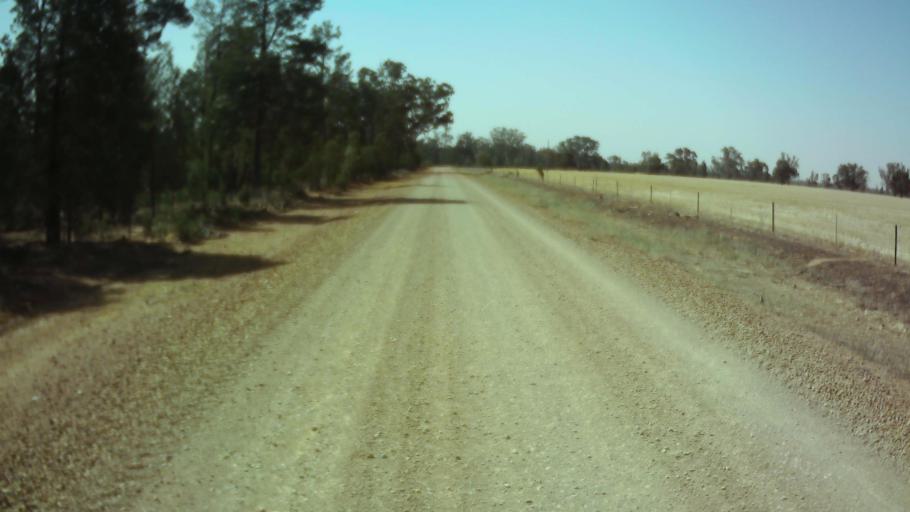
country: AU
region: New South Wales
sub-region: Weddin
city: Grenfell
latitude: -33.9515
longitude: 147.9296
